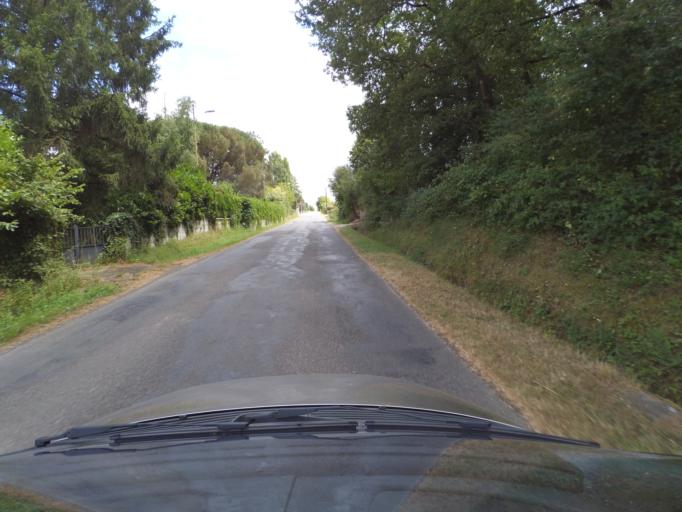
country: FR
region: Centre
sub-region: Departement de l'Indre
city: Belabre
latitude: 46.4654
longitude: 1.0493
